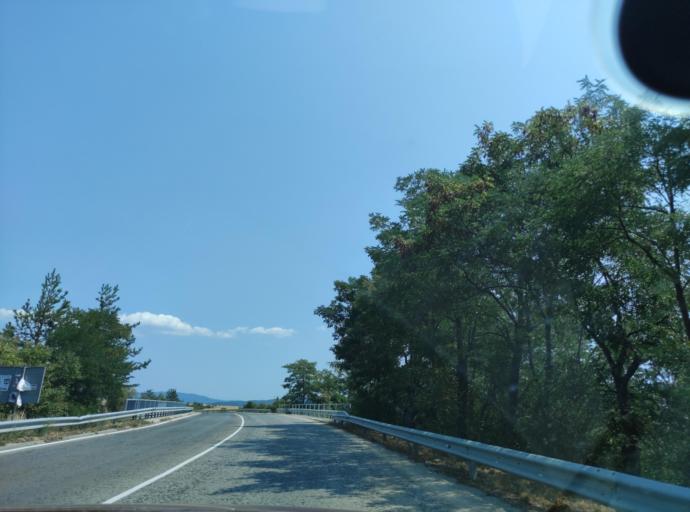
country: BG
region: Blagoevgrad
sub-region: Obshtina Razlog
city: Razlog
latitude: 41.8709
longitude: 23.4753
